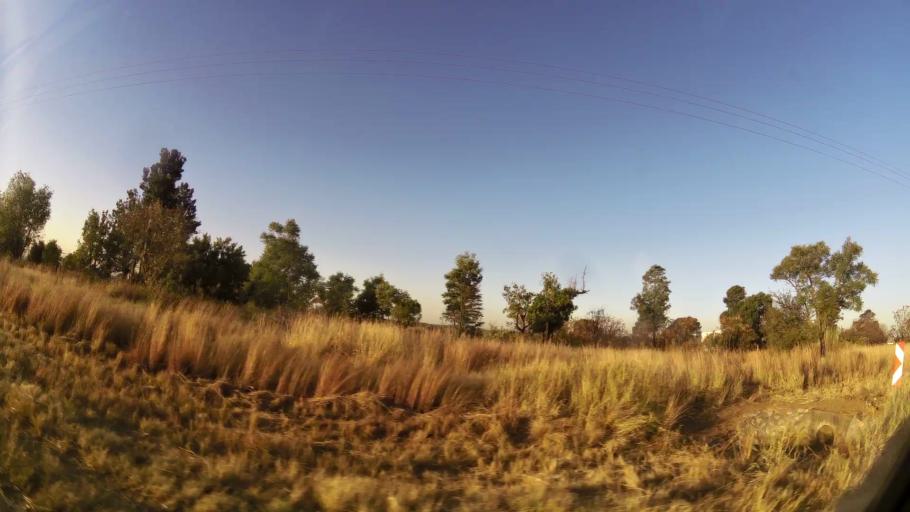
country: ZA
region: Gauteng
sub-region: City of Johannesburg Metropolitan Municipality
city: Diepsloot
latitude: -25.9290
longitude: 28.0440
